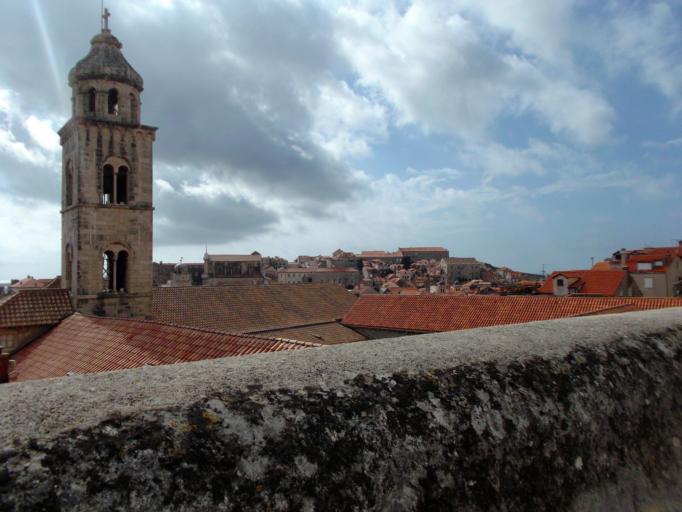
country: HR
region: Dubrovacko-Neretvanska
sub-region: Grad Dubrovnik
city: Dubrovnik
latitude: 42.6393
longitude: 18.1075
